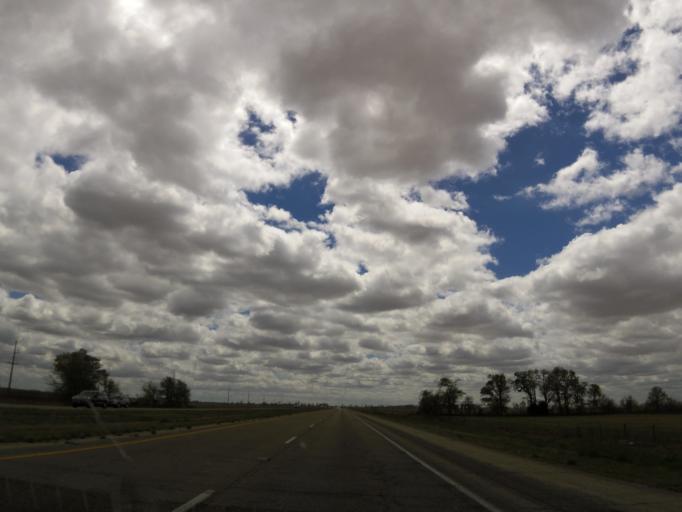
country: US
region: Arkansas
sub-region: Poinsett County
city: Trumann
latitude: 35.6033
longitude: -90.4968
